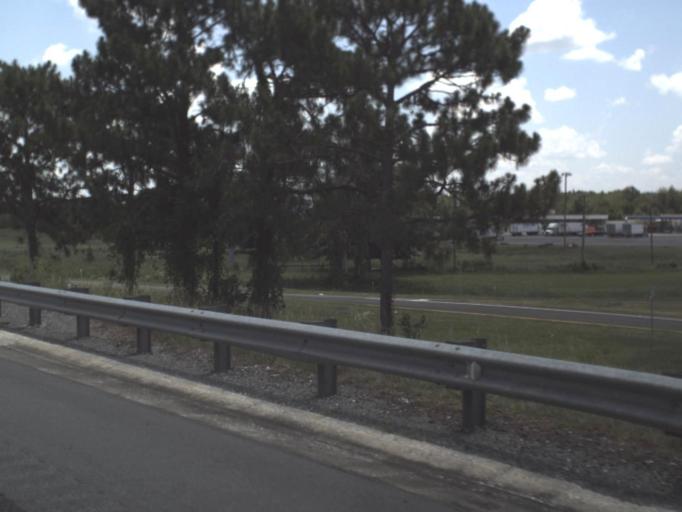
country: US
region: Florida
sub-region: Madison County
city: Madison
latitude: 30.3794
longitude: -83.2969
